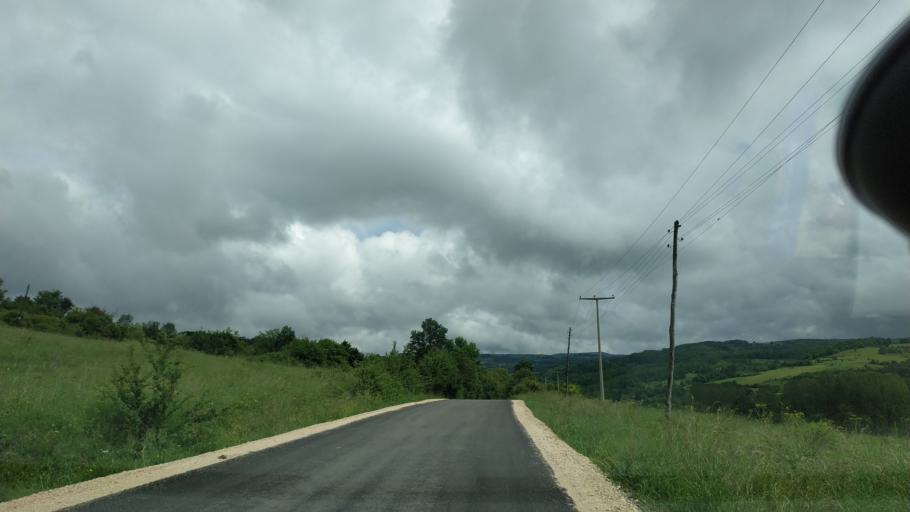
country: RS
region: Central Serbia
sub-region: Zajecarski Okrug
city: Soko Banja
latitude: 43.6515
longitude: 21.9018
